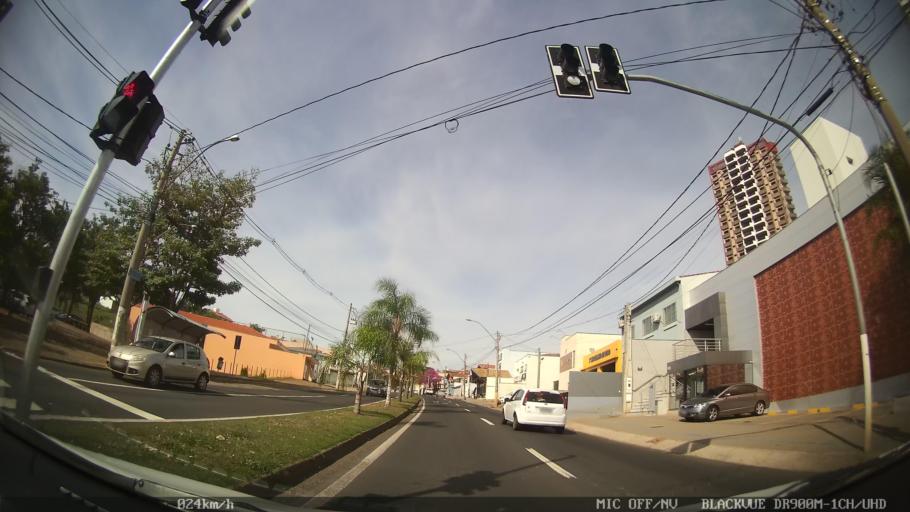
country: BR
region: Sao Paulo
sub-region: Piracicaba
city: Piracicaba
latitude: -22.7296
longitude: -47.6653
